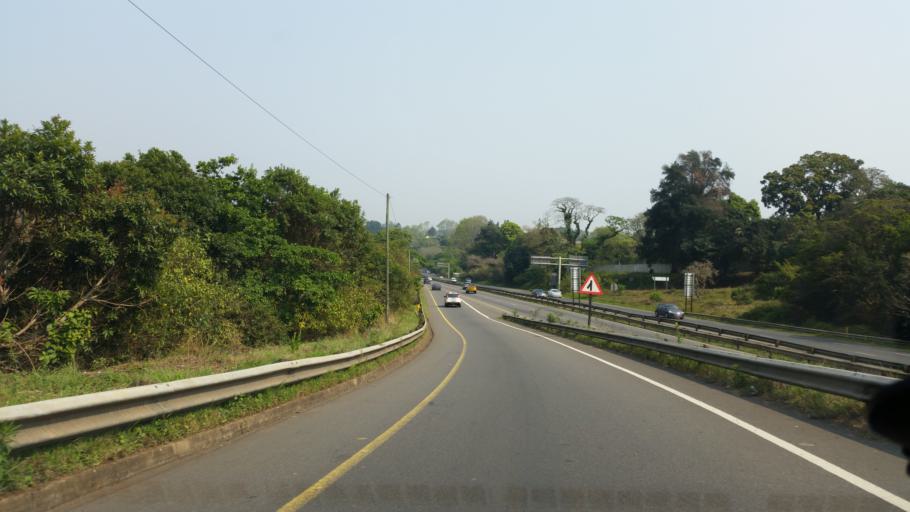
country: ZA
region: KwaZulu-Natal
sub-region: eThekwini Metropolitan Municipality
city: Berea
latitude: -29.7945
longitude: 30.8331
